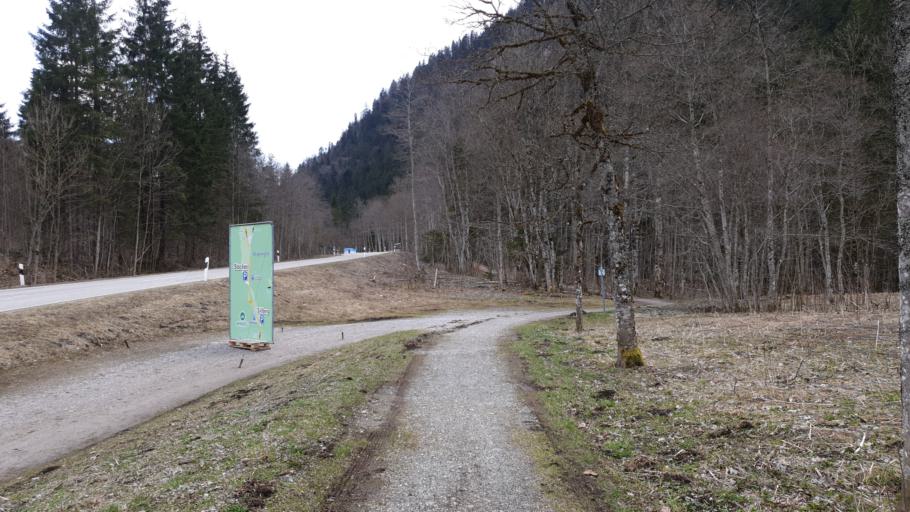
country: DE
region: Bavaria
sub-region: Upper Bavaria
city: Bayrischzell
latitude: 47.6466
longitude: 12.0086
